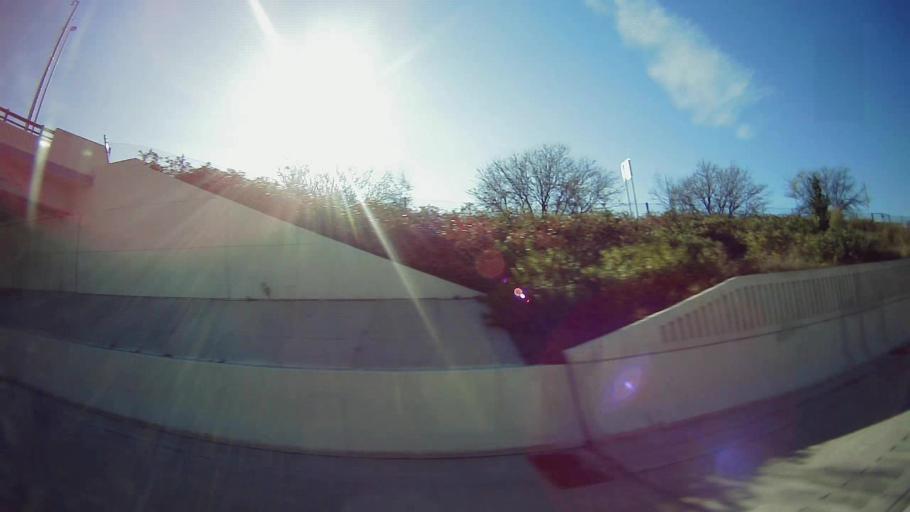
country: US
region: Michigan
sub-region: Wayne County
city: Livonia
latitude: 42.3818
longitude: -83.4009
